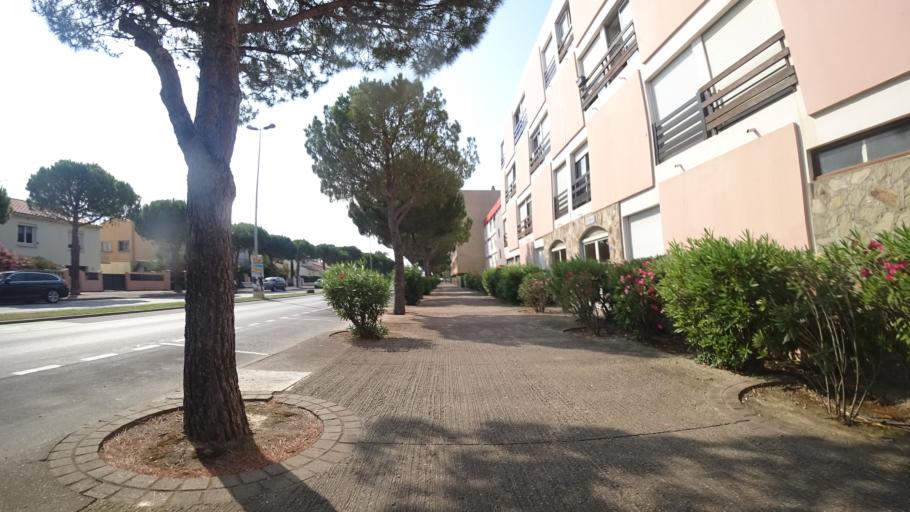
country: FR
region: Languedoc-Roussillon
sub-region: Departement des Pyrenees-Orientales
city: Saint-Cyprien-Plage
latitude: 42.6257
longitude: 3.0341
